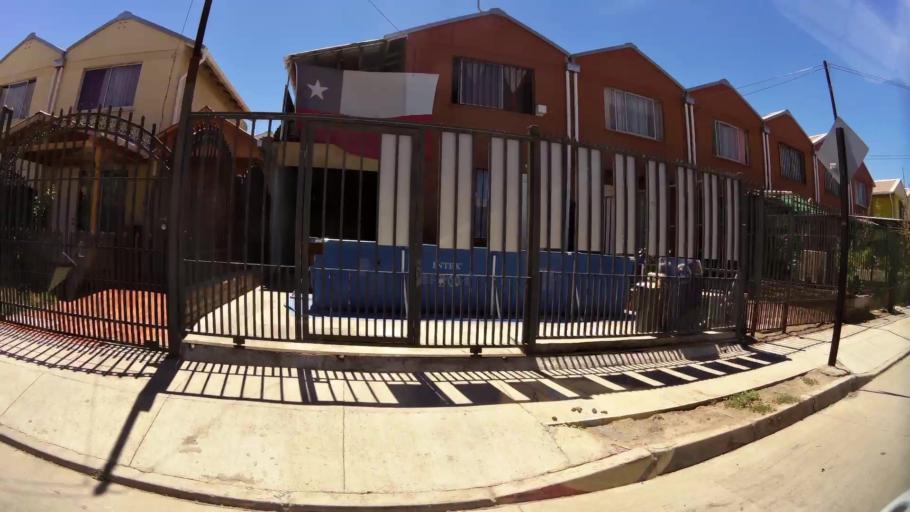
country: CL
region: O'Higgins
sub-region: Provincia de Cachapoal
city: Rancagua
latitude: -34.1538
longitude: -70.7118
